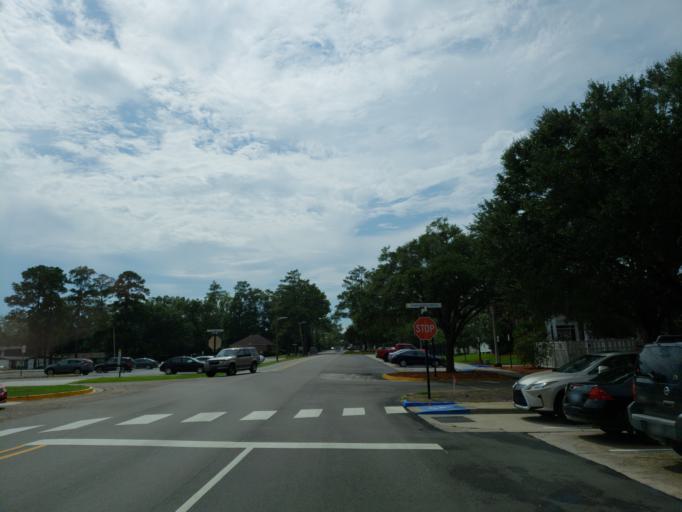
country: US
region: Mississippi
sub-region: Lamar County
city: Arnold Line
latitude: 31.3285
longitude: -89.3394
